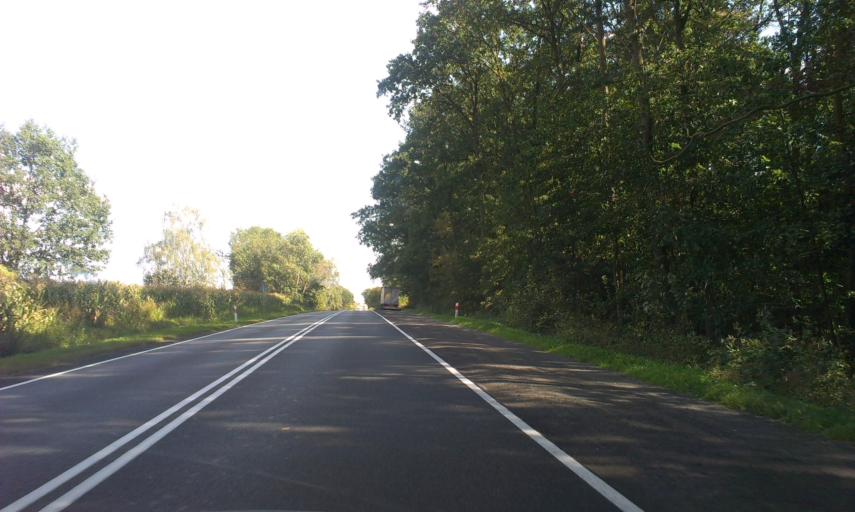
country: PL
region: Greater Poland Voivodeship
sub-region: Powiat pilski
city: Osiek nad Notecia
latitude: 53.1548
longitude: 17.3493
